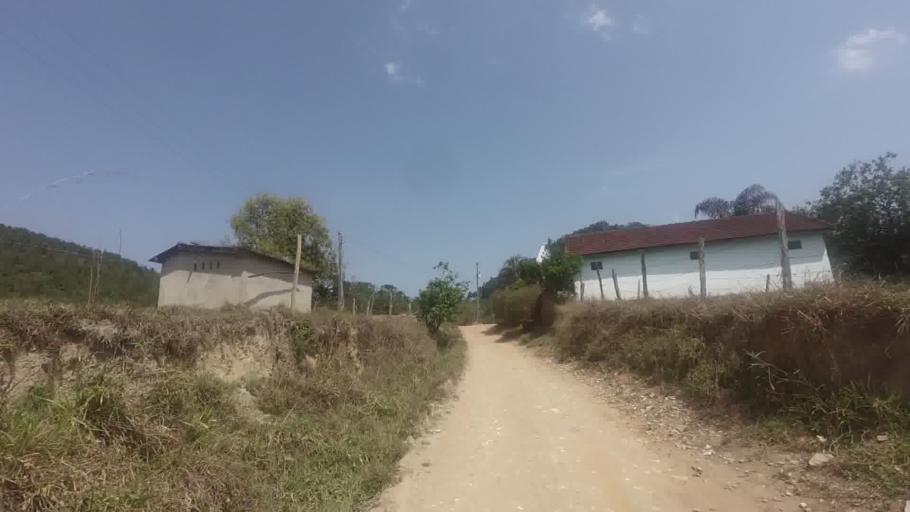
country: BR
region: Espirito Santo
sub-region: Mimoso Do Sul
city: Mimoso do Sul
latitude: -20.9974
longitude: -41.5028
